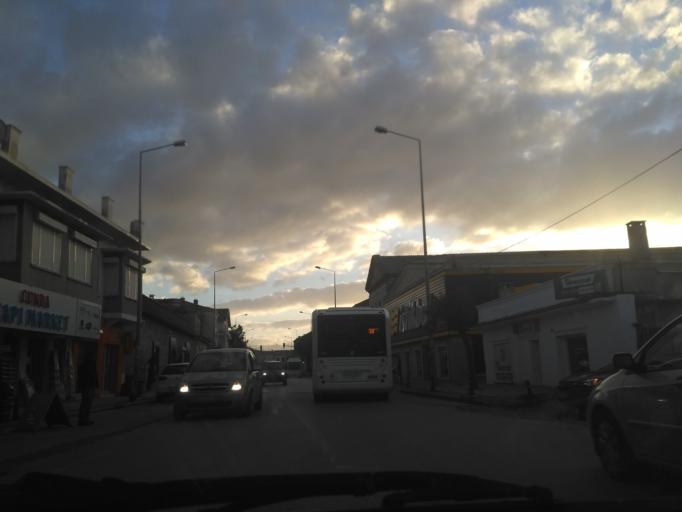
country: TR
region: Balikesir
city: Ayvalik
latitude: 39.3237
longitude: 26.6944
